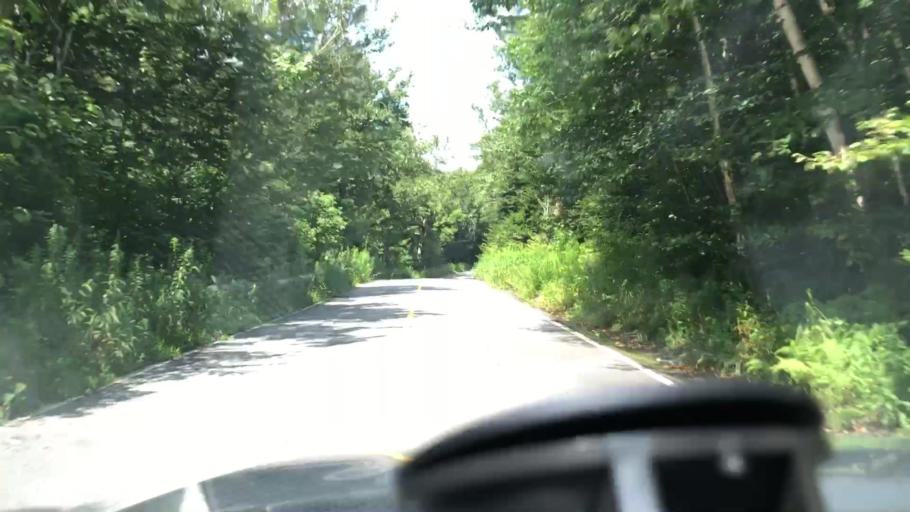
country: US
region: Massachusetts
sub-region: Berkshire County
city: Adams
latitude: 42.6504
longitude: -73.1610
